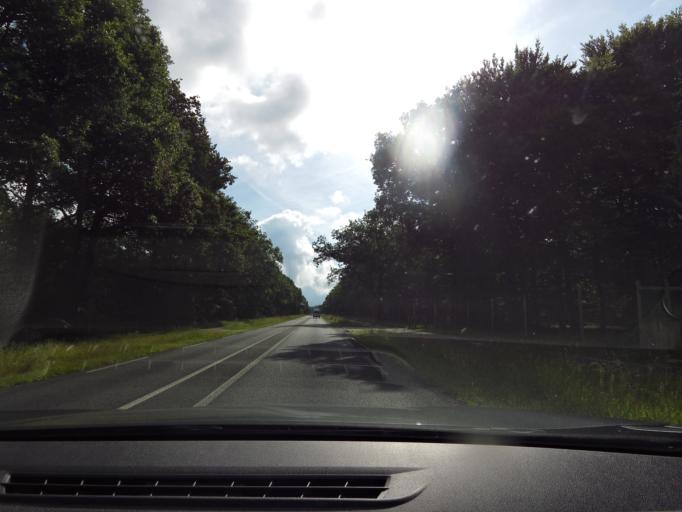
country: NL
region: Gelderland
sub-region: Gemeente Apeldoorn
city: Uddel
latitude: 52.2224
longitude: 5.8143
